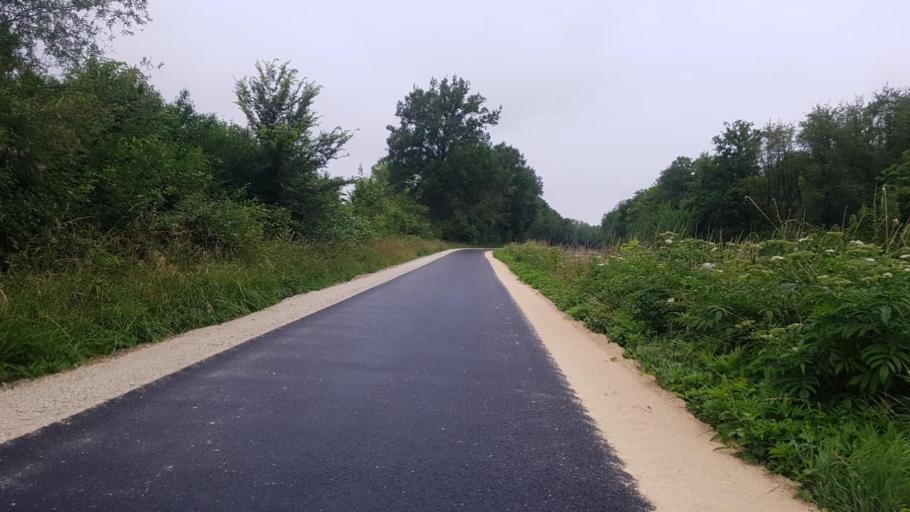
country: FR
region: Champagne-Ardenne
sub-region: Departement de la Marne
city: Vitry-le-Francois
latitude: 48.7970
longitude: 4.5268
